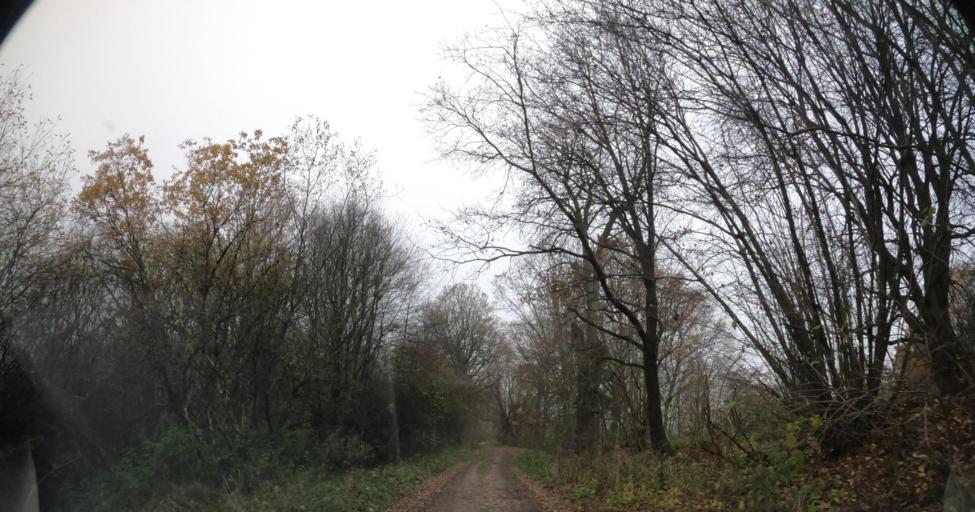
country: PL
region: West Pomeranian Voivodeship
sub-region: Powiat drawski
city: Drawsko Pomorskie
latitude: 53.5891
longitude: 15.7971
